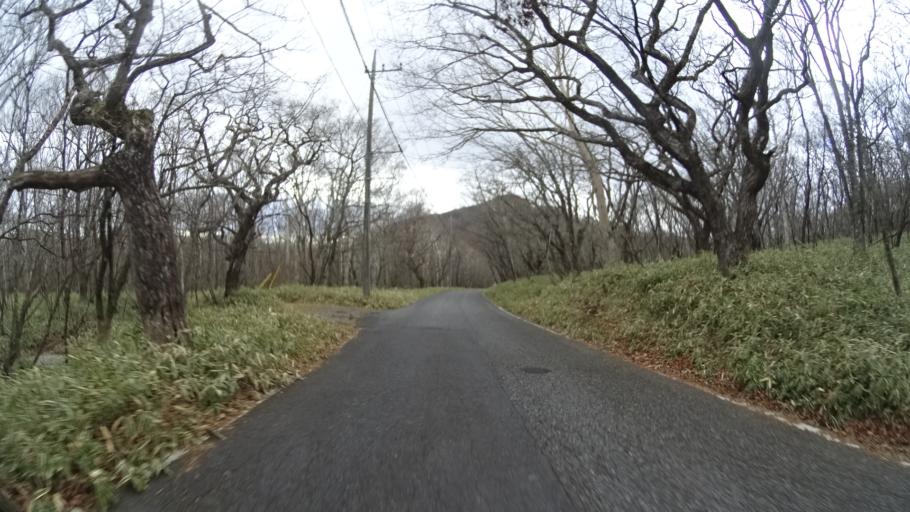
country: JP
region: Gunma
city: Omamacho-omama
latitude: 36.5333
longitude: 139.1759
